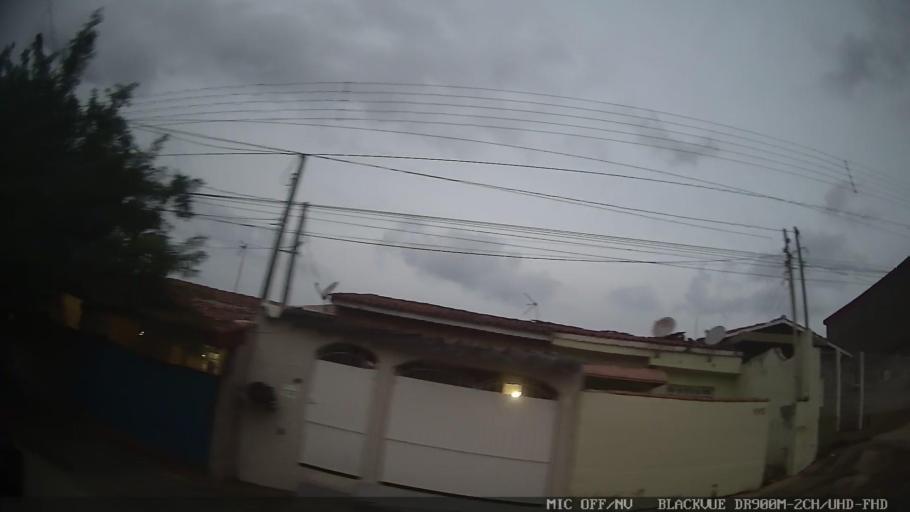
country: BR
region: Sao Paulo
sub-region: Atibaia
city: Atibaia
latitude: -23.1277
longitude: -46.5694
